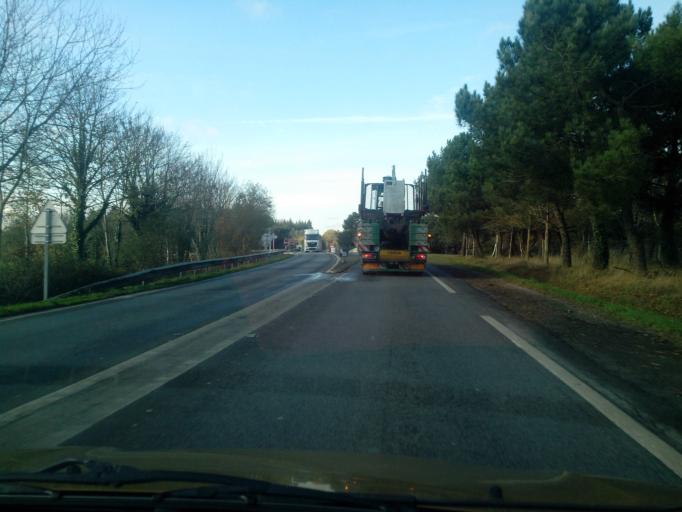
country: FR
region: Brittany
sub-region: Departement du Morbihan
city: Molac
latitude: 47.7796
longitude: -2.4575
